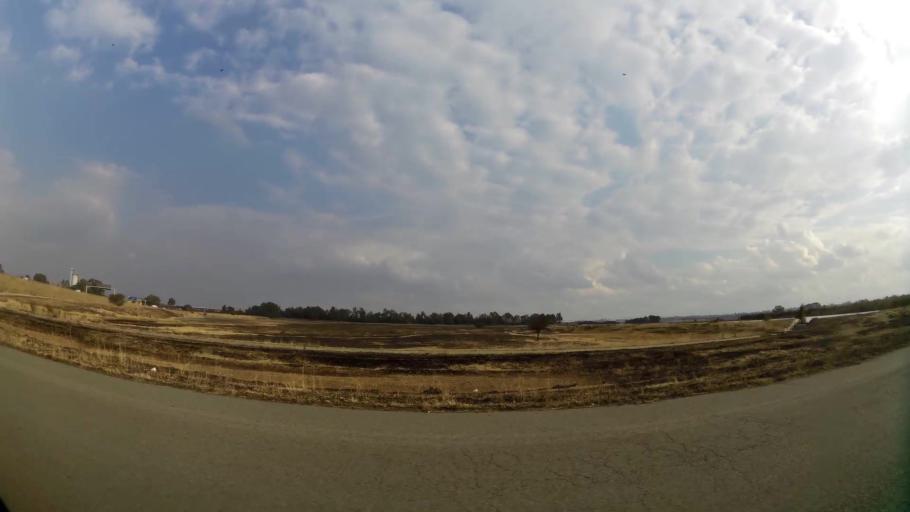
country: ZA
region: Gauteng
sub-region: Sedibeng District Municipality
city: Vereeniging
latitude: -26.6779
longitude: 27.9026
